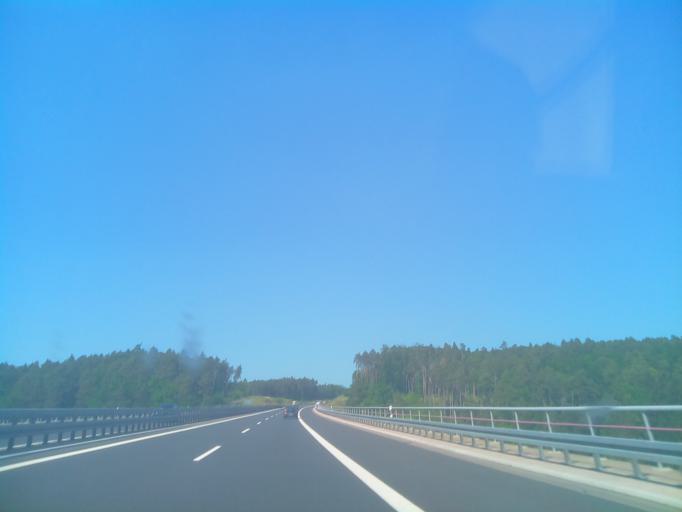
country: DE
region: Bavaria
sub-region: Regierungsbezirk Unterfranken
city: Oberstreu
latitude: 50.3903
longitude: 10.3135
